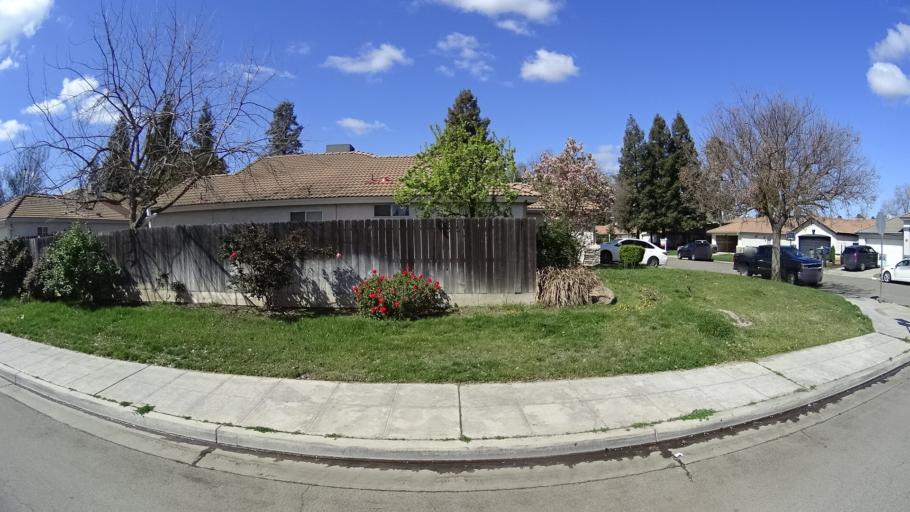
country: US
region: California
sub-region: Fresno County
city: West Park
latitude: 36.8257
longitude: -119.8941
